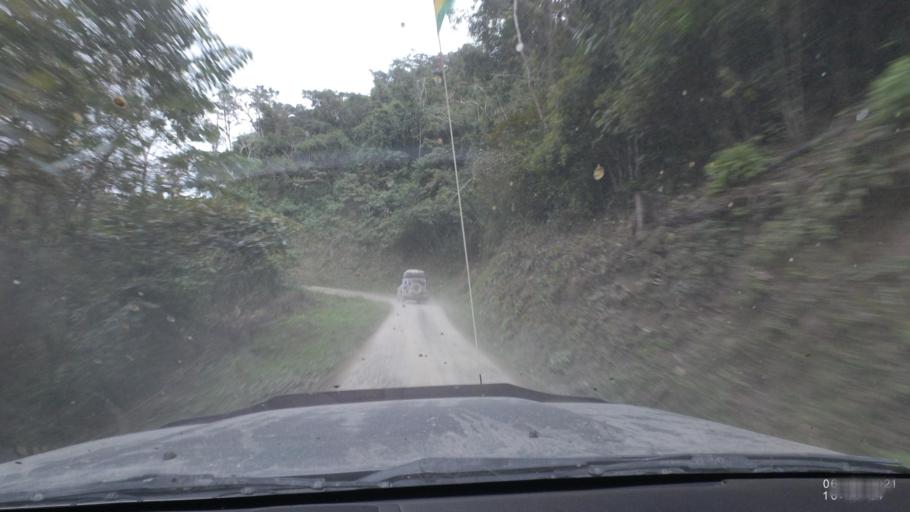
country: BO
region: La Paz
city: Quime
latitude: -16.5229
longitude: -66.7686
